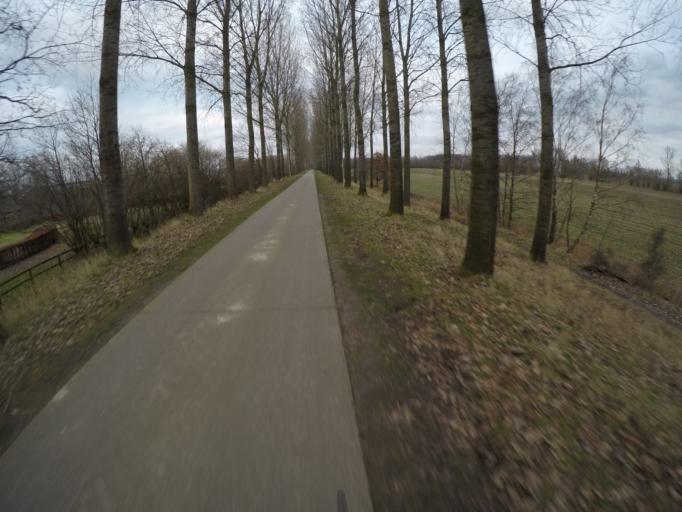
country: BE
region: Flanders
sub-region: Provincie Oost-Vlaanderen
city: Sint-Gillis-Waas
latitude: 51.2425
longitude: 4.1371
